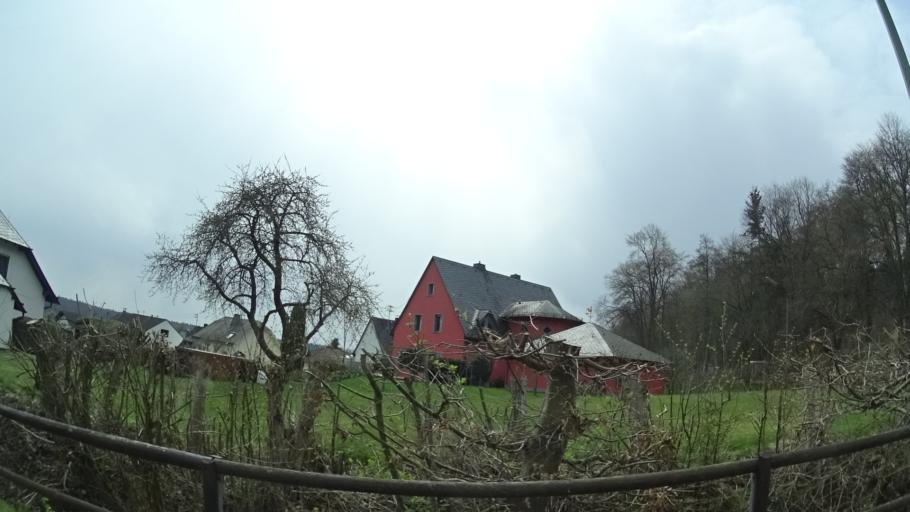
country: DE
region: Rheinland-Pfalz
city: Stipshausen
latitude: 49.8493
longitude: 7.2864
